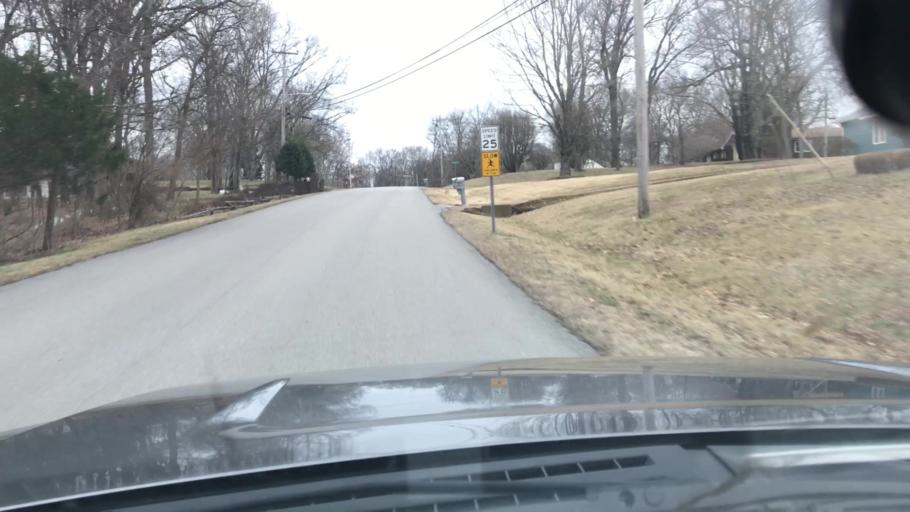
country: US
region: Tennessee
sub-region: Williamson County
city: Brentwood Estates
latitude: 36.0063
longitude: -86.7194
